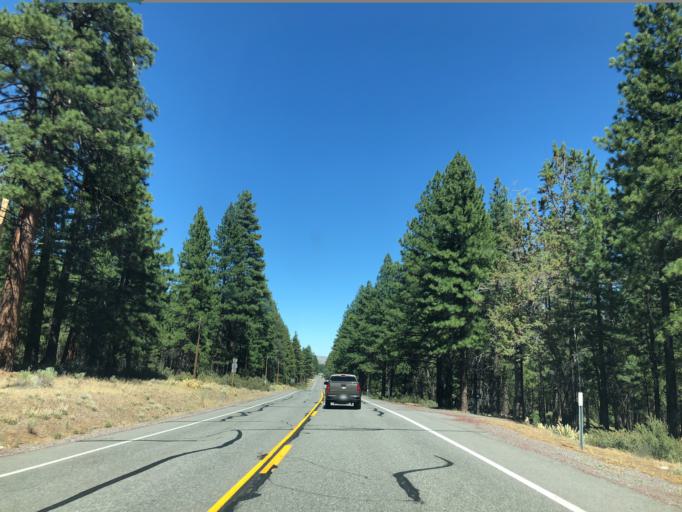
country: US
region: California
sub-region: Lassen County
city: Susanville
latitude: 40.4150
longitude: -120.7253
